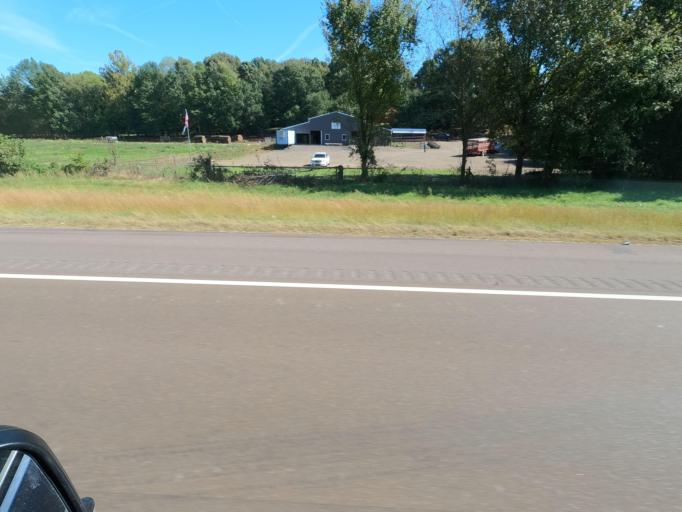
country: US
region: Tennessee
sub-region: Dyer County
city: Dyersburg
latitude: 36.0136
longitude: -89.3409
